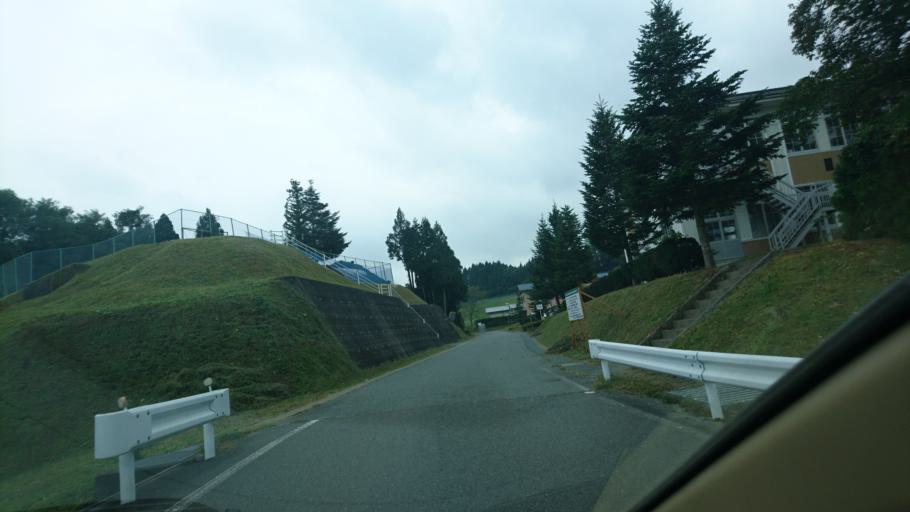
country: JP
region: Iwate
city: Ichinoseki
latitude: 38.9207
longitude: 141.3433
